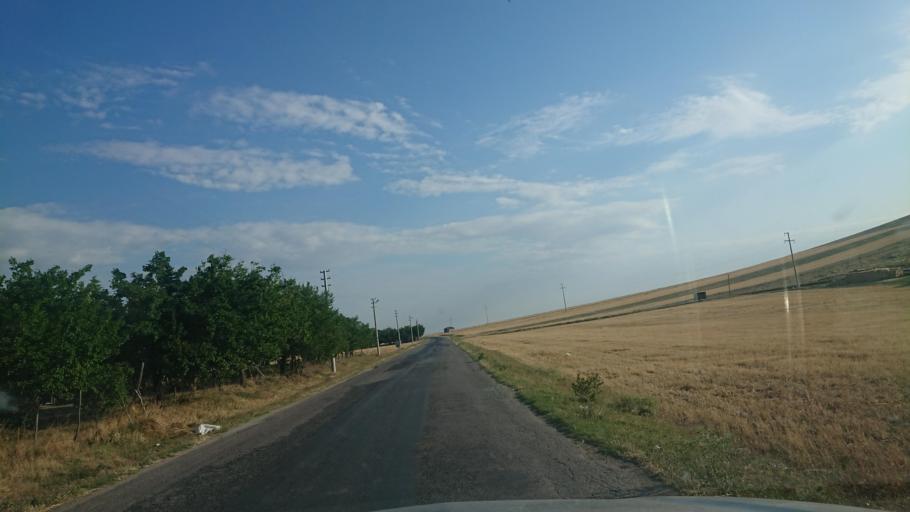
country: TR
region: Aksaray
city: Ortakoy
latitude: 38.7728
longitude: 34.0618
